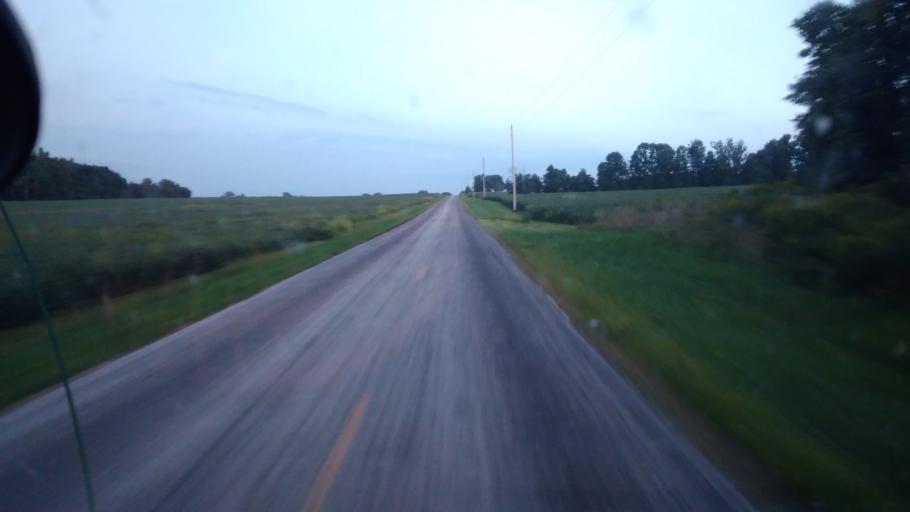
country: US
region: Ohio
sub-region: Hardin County
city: Kenton
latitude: 40.6353
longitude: -83.4575
